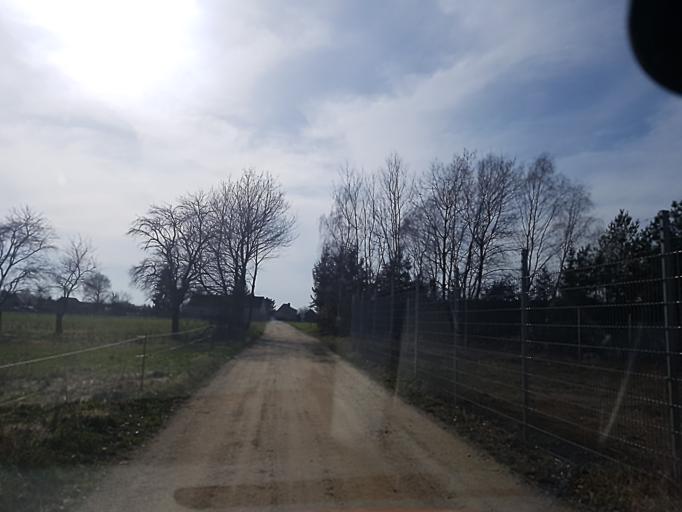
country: DE
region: Brandenburg
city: Sallgast
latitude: 51.6199
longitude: 13.8125
